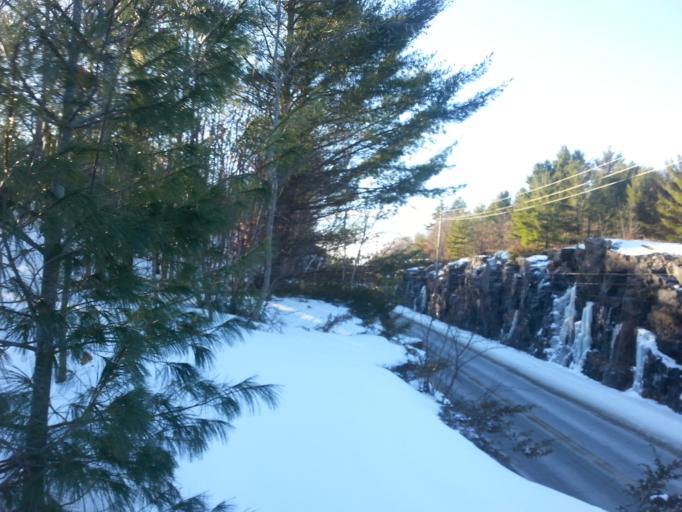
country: CA
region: Ontario
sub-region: Parry Sound District
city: Parry Sound
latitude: 45.3603
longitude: -80.0319
